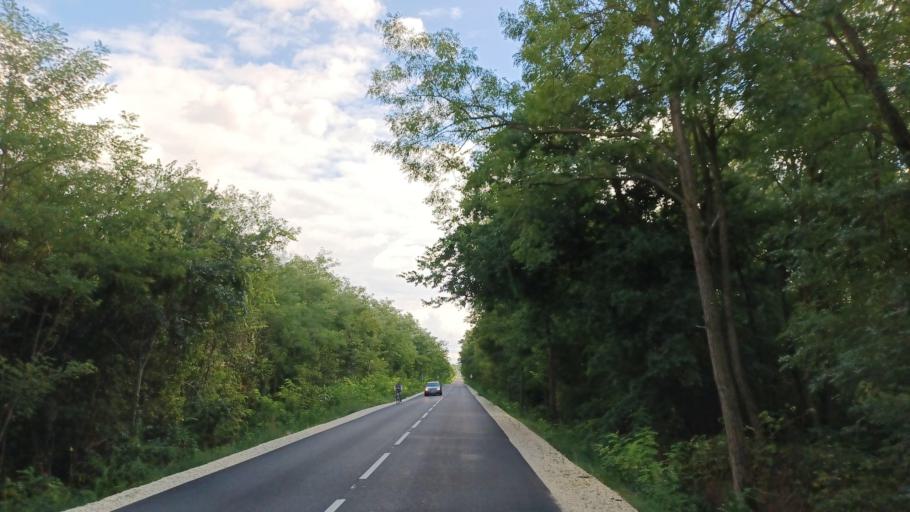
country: HU
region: Tolna
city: Nagydorog
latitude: 46.6115
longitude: 18.6827
